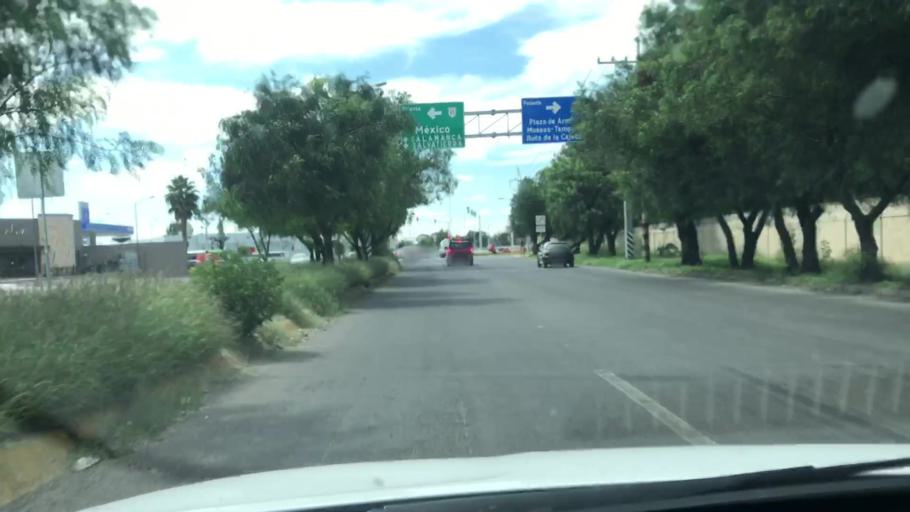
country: MX
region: Guanajuato
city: Celaya
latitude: 20.5171
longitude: -100.7798
